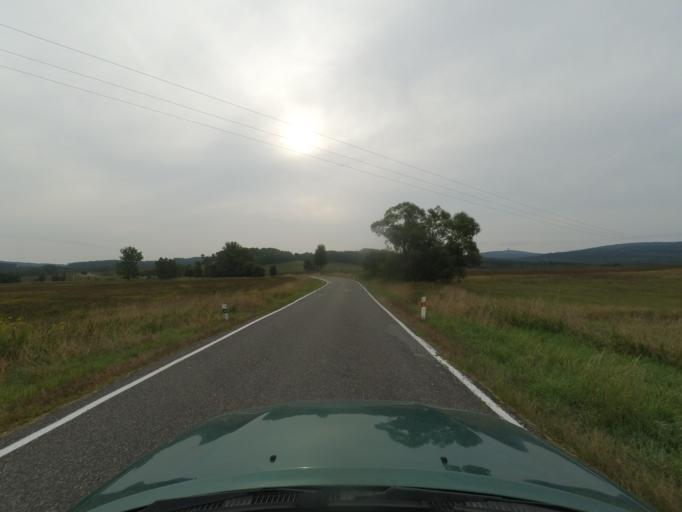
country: DE
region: Bavaria
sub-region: Upper Palatinate
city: Eslarn
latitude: 49.5872
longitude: 12.5964
